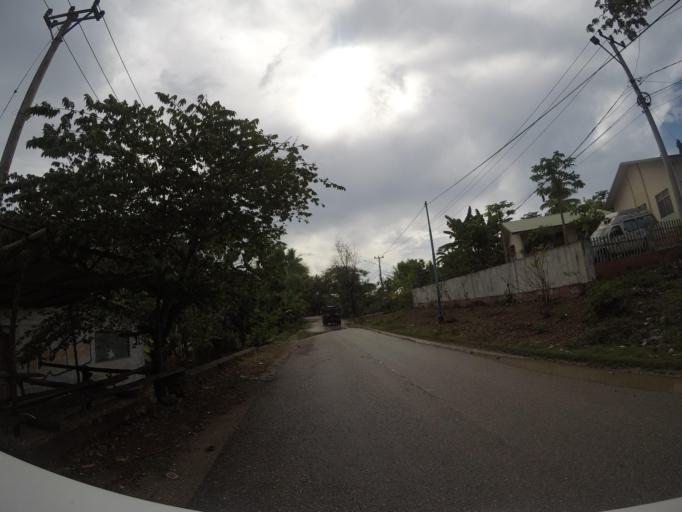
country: TL
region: Baucau
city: Baucau
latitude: -8.4810
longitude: 126.4584
